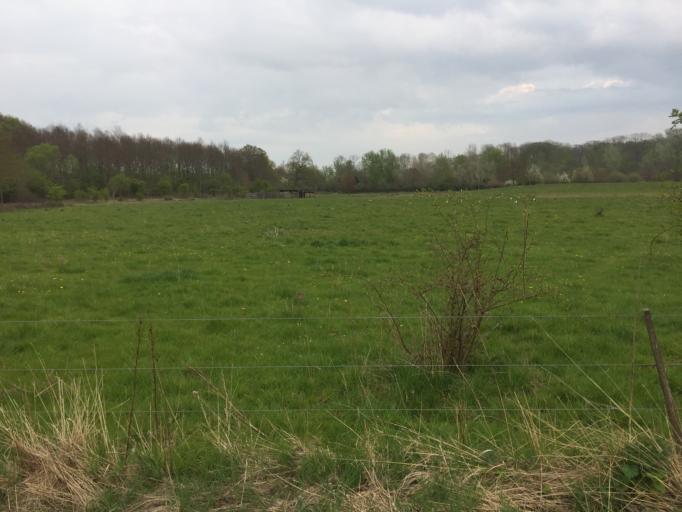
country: DK
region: South Denmark
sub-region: Odense Kommune
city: Hojby
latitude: 55.3533
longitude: 10.4373
